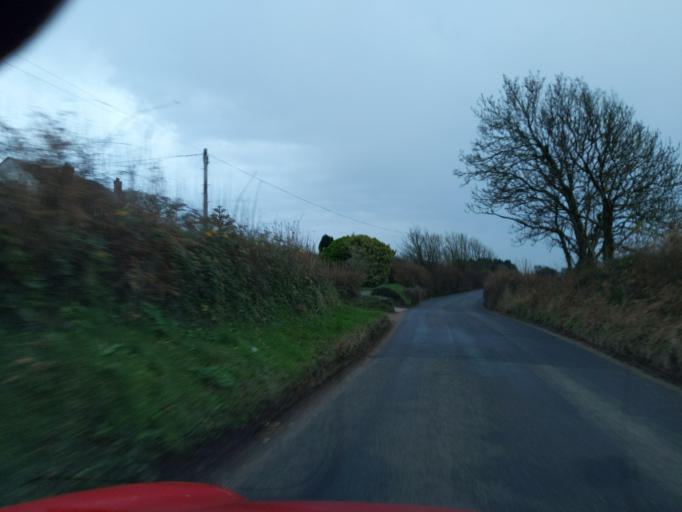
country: GB
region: England
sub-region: Devon
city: Wembury
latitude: 50.3313
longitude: -4.0641
